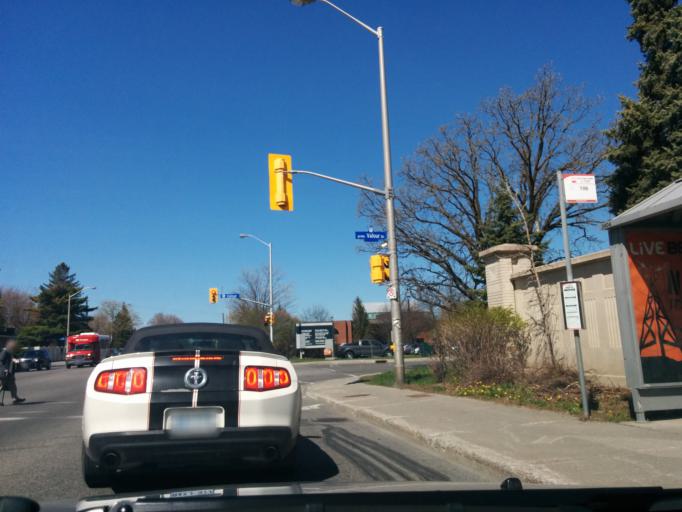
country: CA
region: Ontario
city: Ottawa
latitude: 45.3987
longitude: -75.6582
